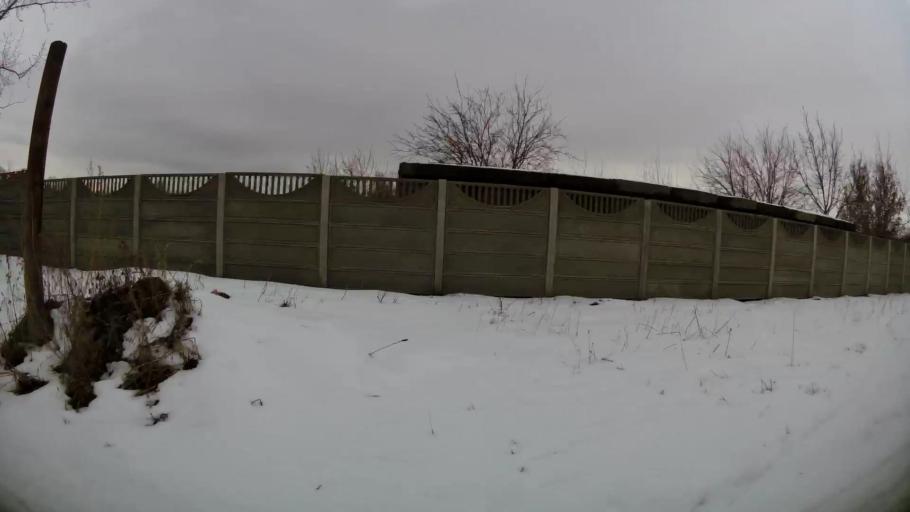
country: RO
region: Ilfov
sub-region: Comuna Pantelimon
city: Pantelimon
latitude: 44.4529
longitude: 26.2186
